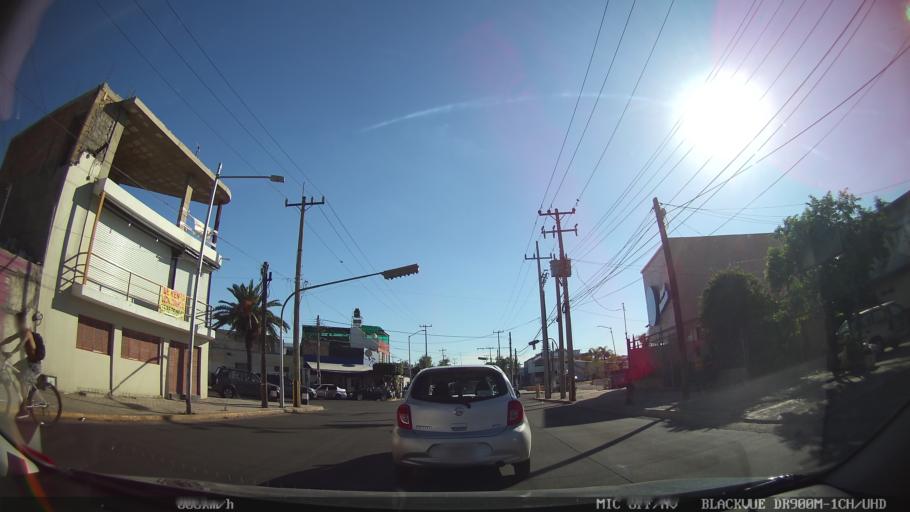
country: MX
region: Jalisco
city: Tlaquepaque
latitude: 20.7099
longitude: -103.3100
